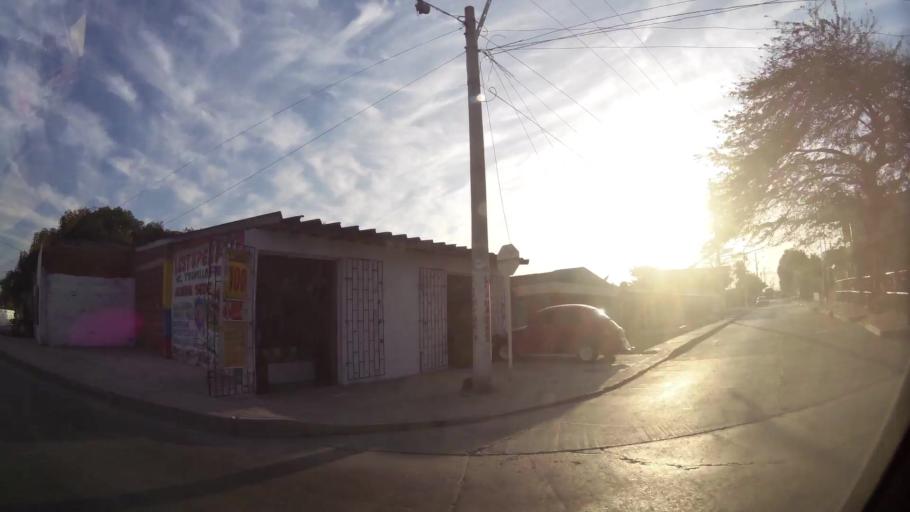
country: CO
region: Atlantico
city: Barranquilla
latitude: 10.9567
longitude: -74.8238
